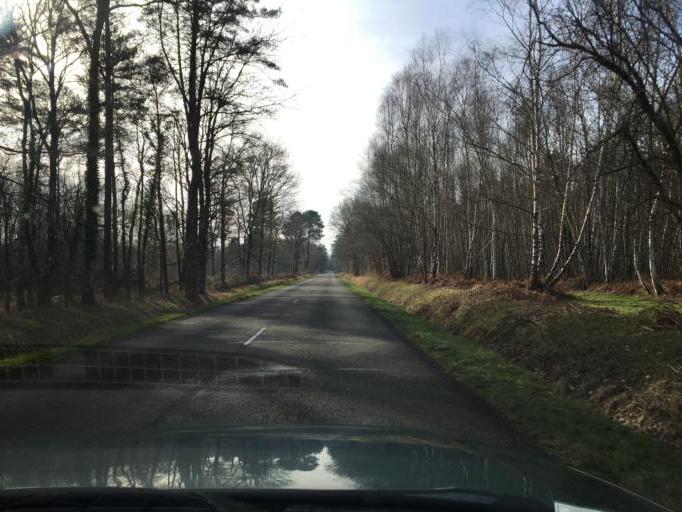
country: FR
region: Centre
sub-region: Departement du Loiret
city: Jouy-le-Potier
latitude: 47.7076
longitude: 1.8523
